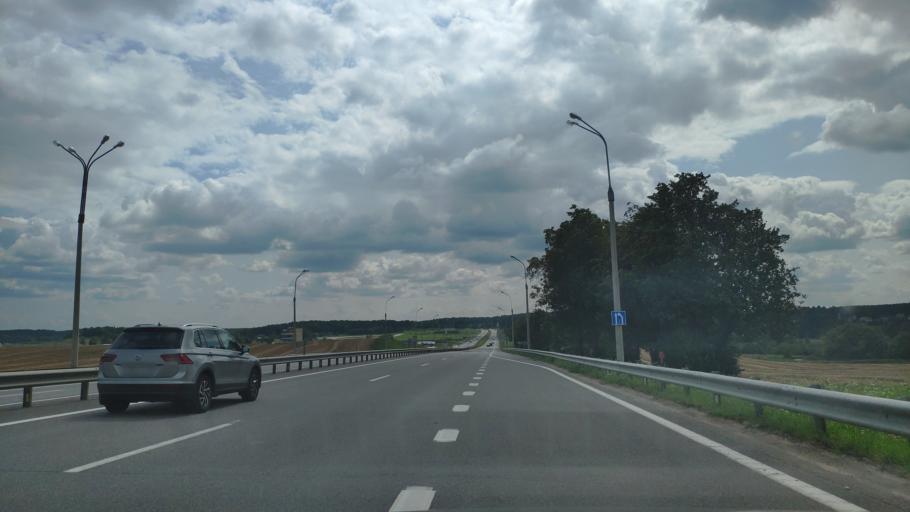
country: BY
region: Minsk
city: Zaslawye
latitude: 54.0053
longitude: 27.3087
